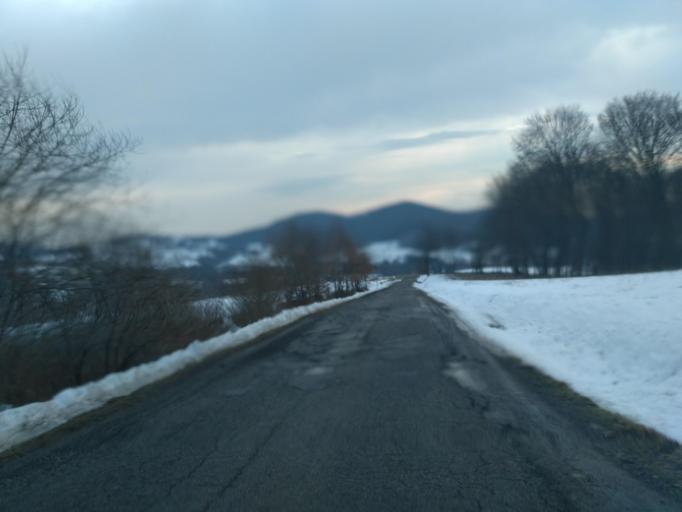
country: PL
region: Subcarpathian Voivodeship
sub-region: Powiat brzozowski
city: Dydnia
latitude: 49.6410
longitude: 22.1625
